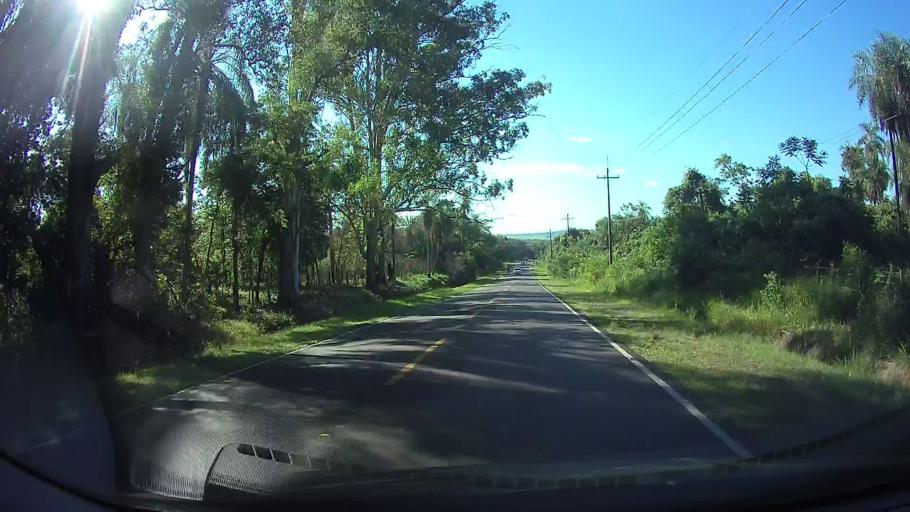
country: PY
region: Cordillera
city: Atyra
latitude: -25.3080
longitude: -57.1542
